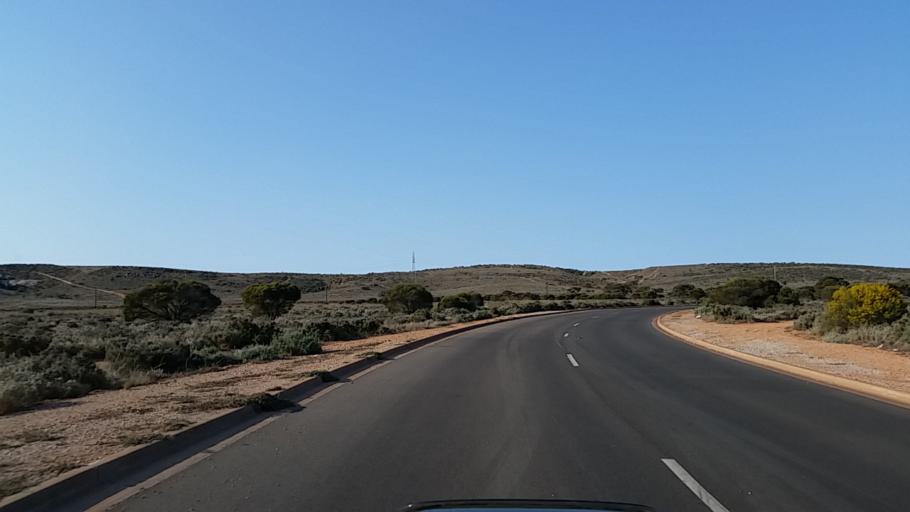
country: AU
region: South Australia
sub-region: Whyalla
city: Whyalla
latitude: -33.0098
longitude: 137.5282
